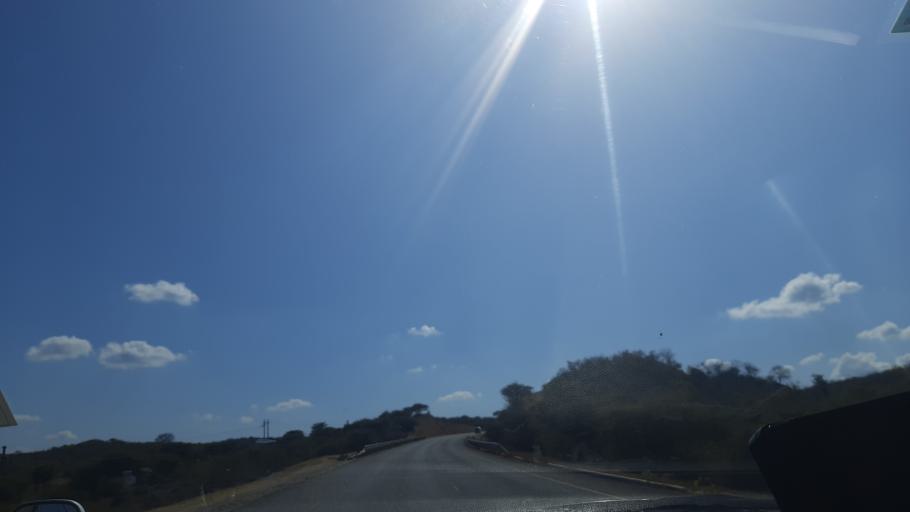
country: TZ
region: Singida
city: Kilimatinde
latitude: -5.7823
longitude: 34.8860
